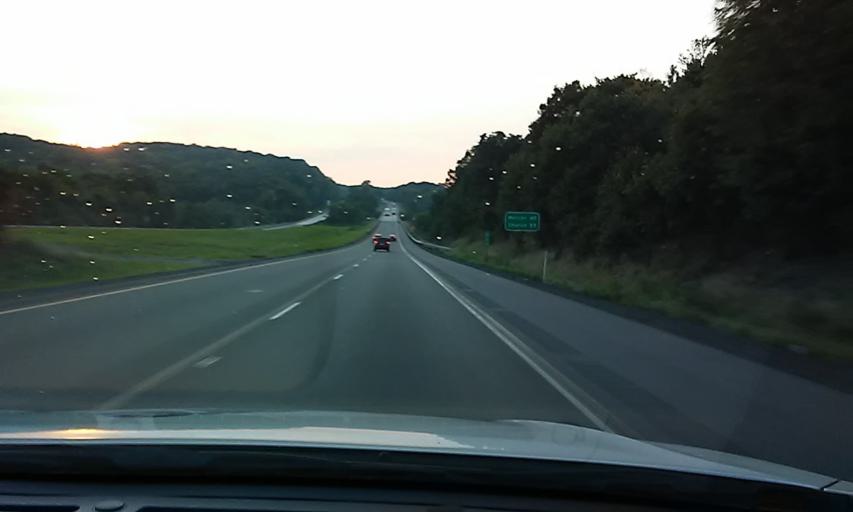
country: US
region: Pennsylvania
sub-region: Clarion County
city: Knox
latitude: 41.1876
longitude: -79.5586
